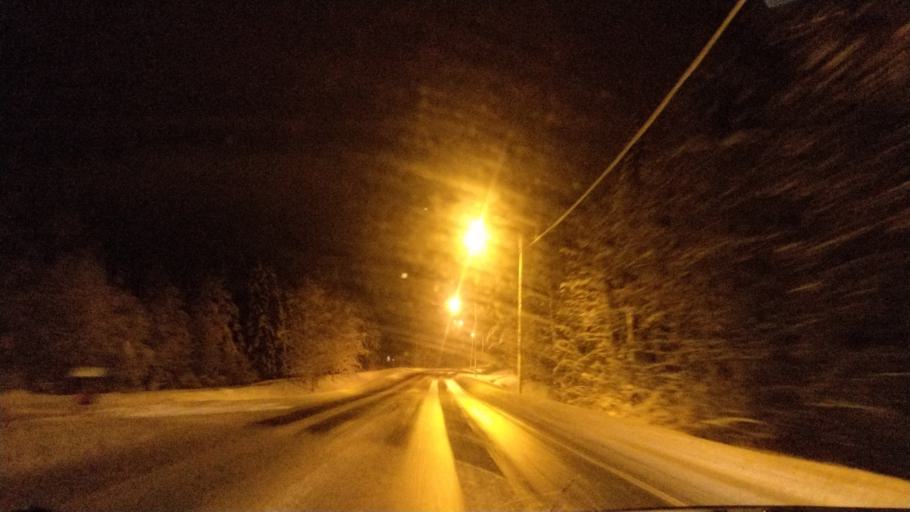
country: FI
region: Lapland
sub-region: Rovaniemi
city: Rovaniemi
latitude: 66.4001
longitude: 25.3881
